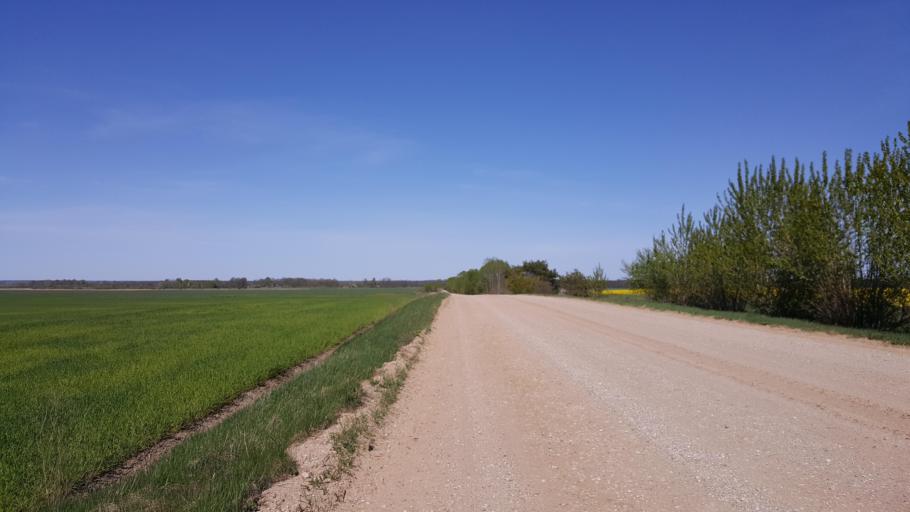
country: BY
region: Brest
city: Kamyanyets
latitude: 52.4131
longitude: 23.8570
